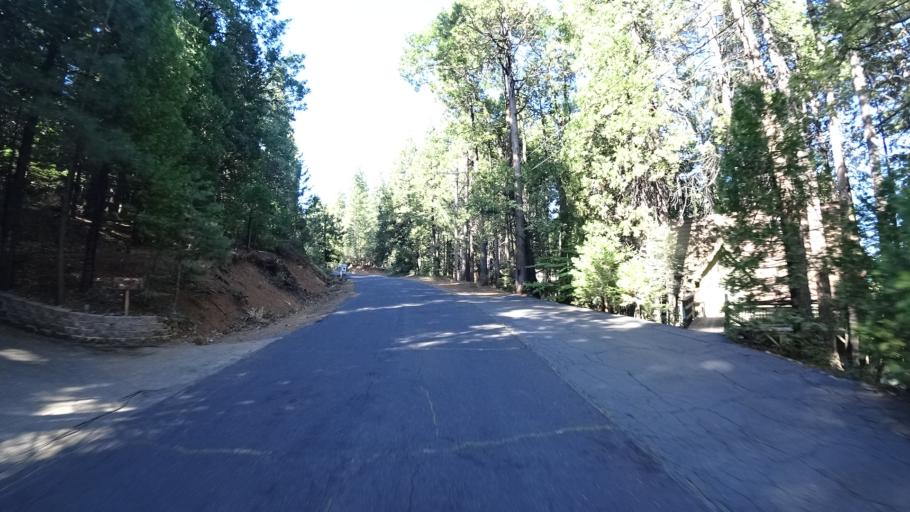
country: US
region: California
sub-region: Calaveras County
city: Arnold
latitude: 38.2534
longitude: -120.3203
